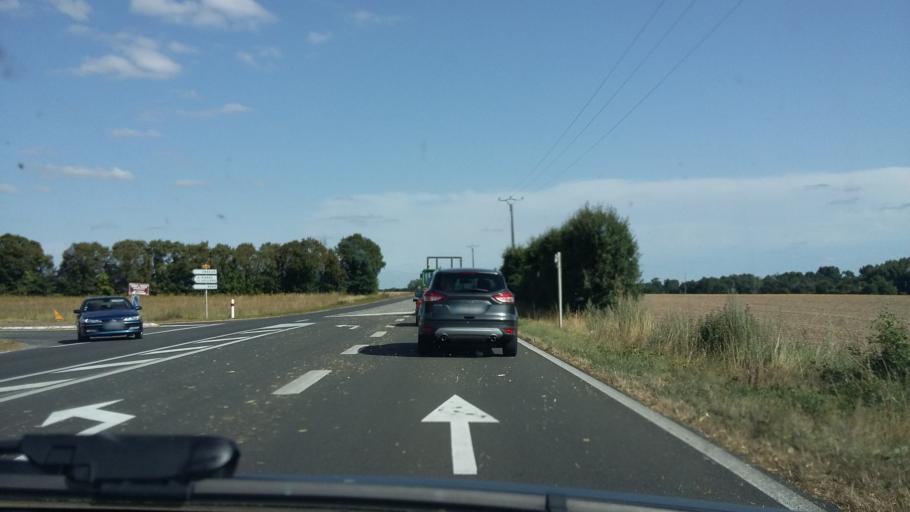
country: FR
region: Poitou-Charentes
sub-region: Departement de la Charente-Maritime
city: Saint-Jean-d'Angely
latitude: 45.9218
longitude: -0.4534
